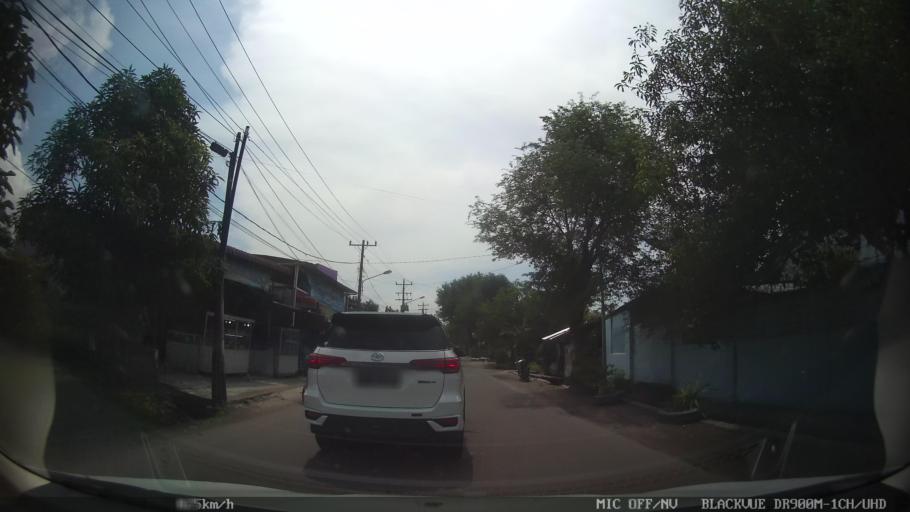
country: ID
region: North Sumatra
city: Labuhan Deli
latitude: 3.6574
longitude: 98.6677
